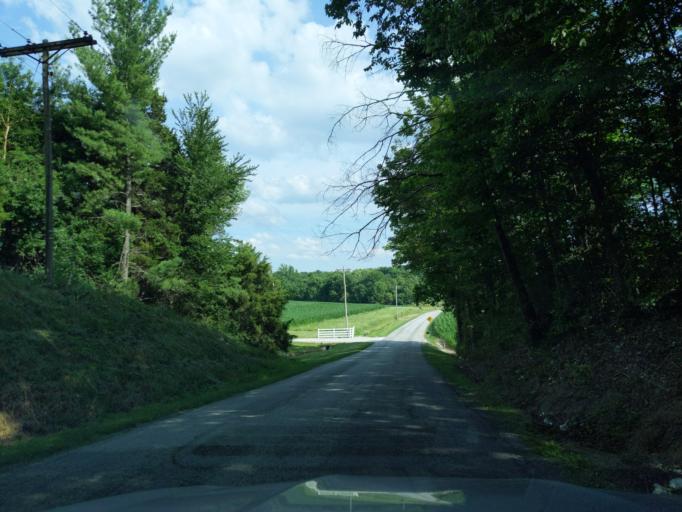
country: US
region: Indiana
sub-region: Decatur County
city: Greensburg
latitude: 39.2910
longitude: -85.4687
